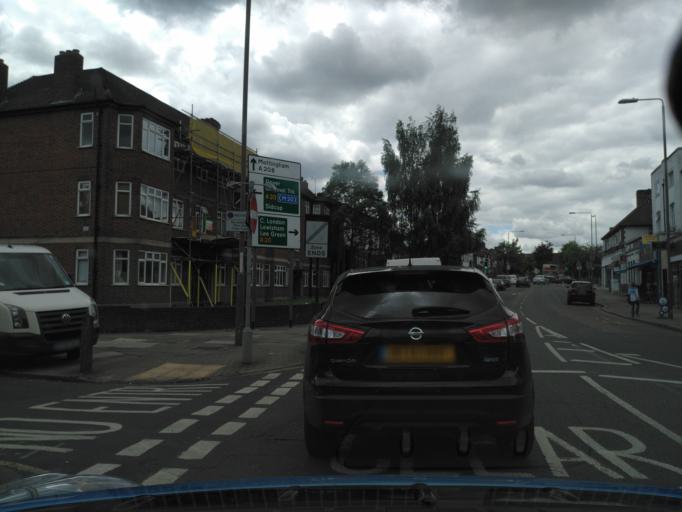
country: GB
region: England
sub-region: Greater London
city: Chislehurst
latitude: 51.4398
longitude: 0.0513
